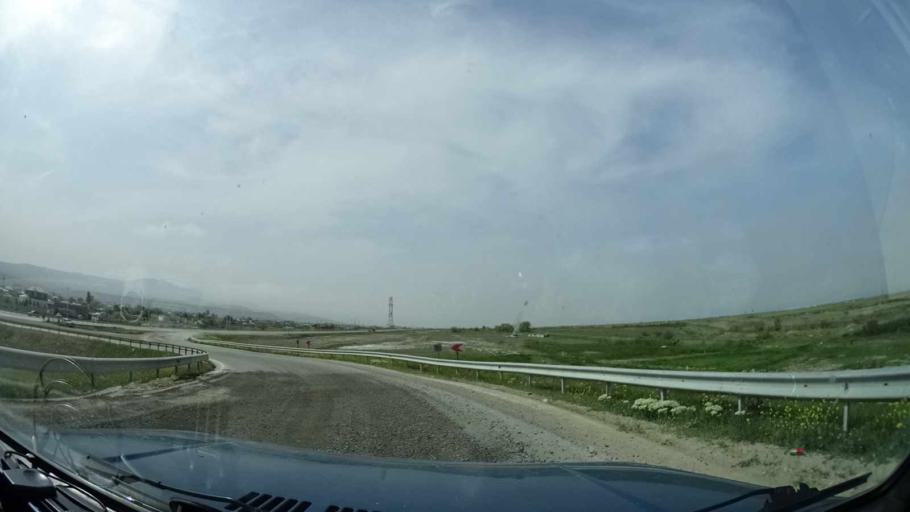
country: AZ
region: Xizi
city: Kilyazi
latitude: 40.8703
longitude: 49.3547
